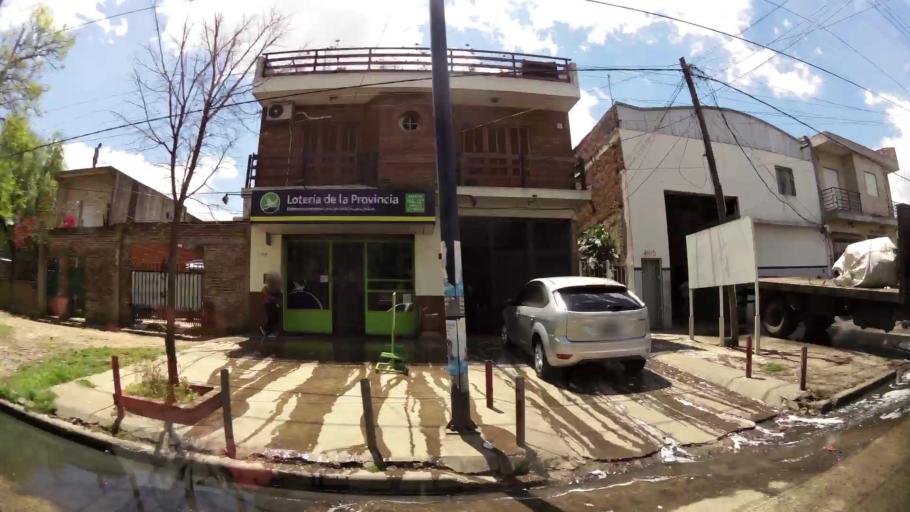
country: AR
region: Buenos Aires
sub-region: Partido de Lanus
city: Lanus
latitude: -34.6935
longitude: -58.4339
